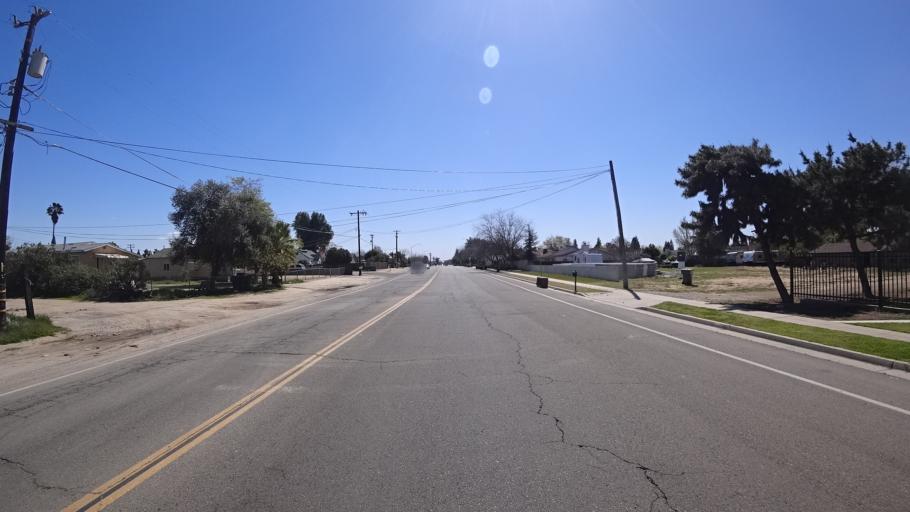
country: US
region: California
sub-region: Fresno County
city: West Park
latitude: 36.7764
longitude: -119.8624
